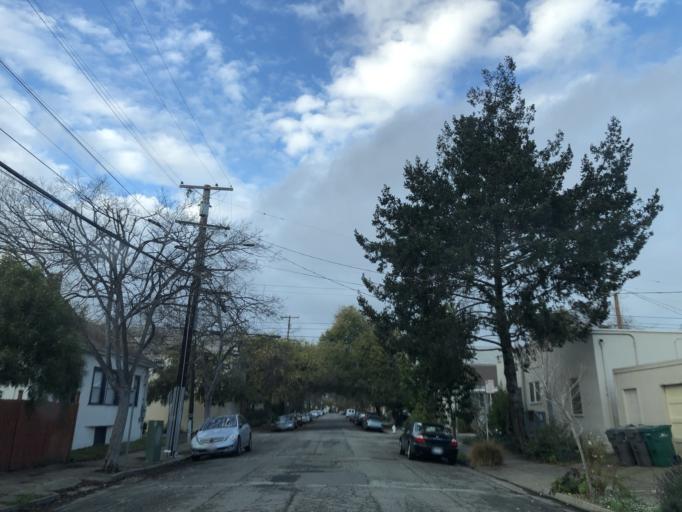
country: US
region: California
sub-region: Alameda County
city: Berkeley
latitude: 37.8456
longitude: -122.2594
